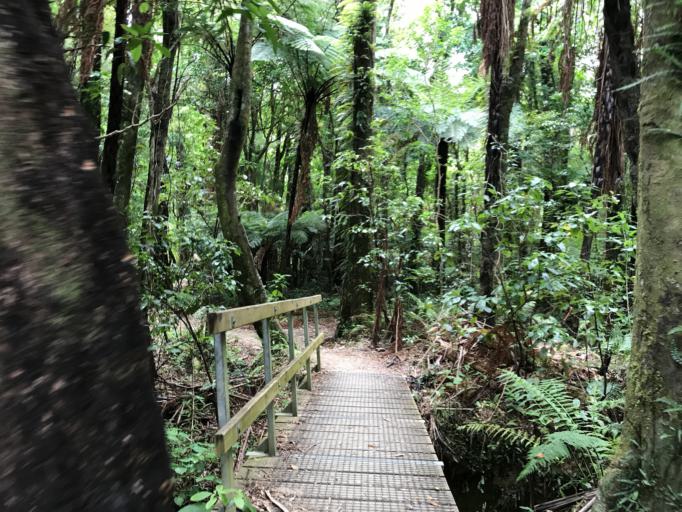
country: NZ
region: Marlborough
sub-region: Marlborough District
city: Picton
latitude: -41.0936
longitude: 174.1882
